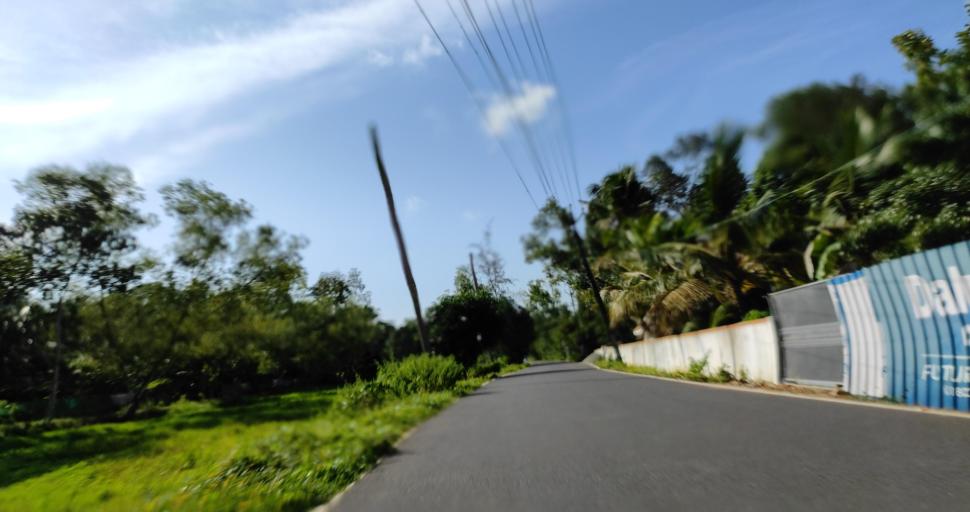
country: IN
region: Kerala
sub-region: Alappuzha
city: Shertallai
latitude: 9.6102
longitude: 76.3335
